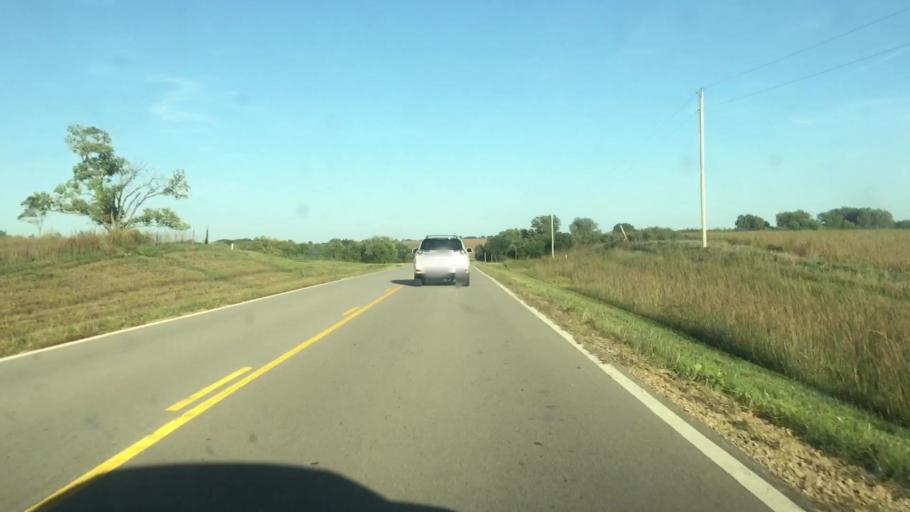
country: US
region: Kansas
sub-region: Brown County
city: Horton
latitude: 39.5874
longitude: -95.5376
